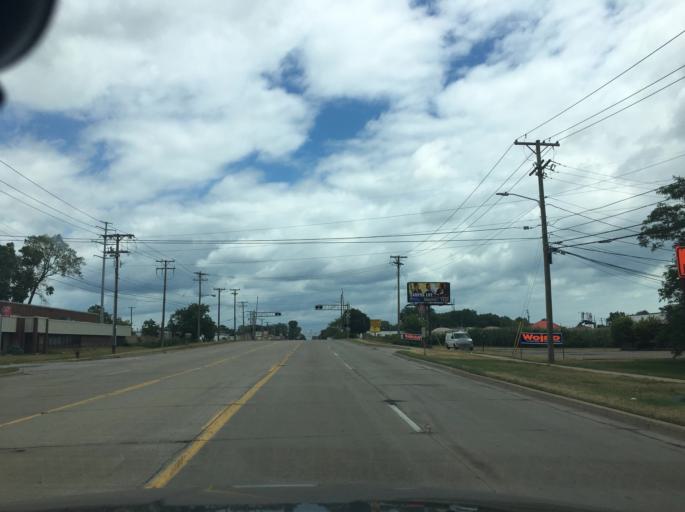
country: US
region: Michigan
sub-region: Macomb County
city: Fraser
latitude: 42.5240
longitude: -82.9508
